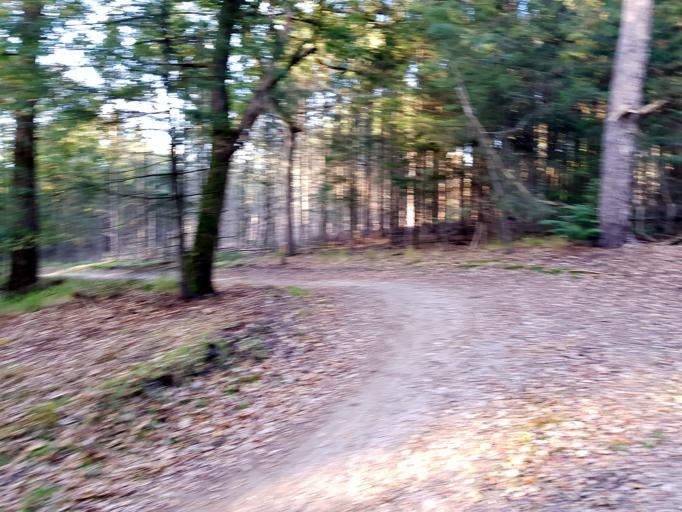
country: NL
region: Gelderland
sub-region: Gemeente Groesbeek
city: Berg en Dal
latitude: 51.7968
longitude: 5.8991
